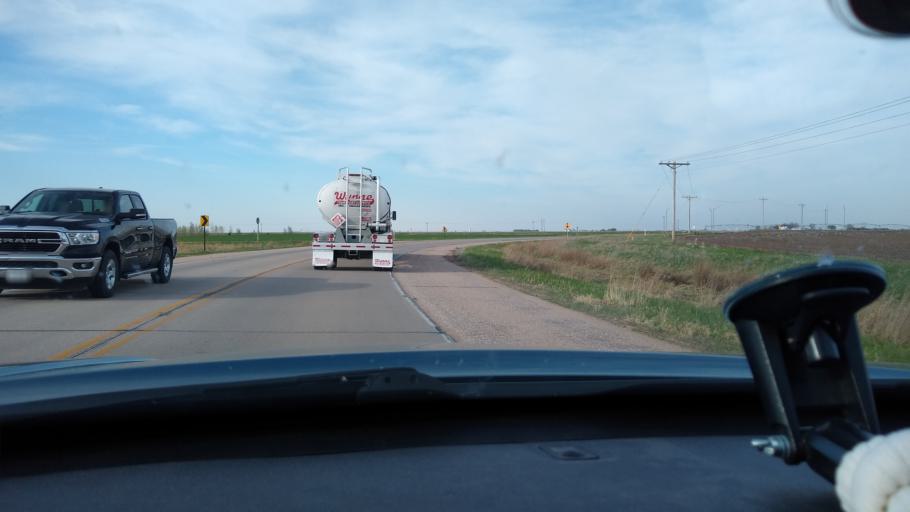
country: US
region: Nebraska
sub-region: Fillmore County
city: Geneva
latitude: 40.5547
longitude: -97.5956
